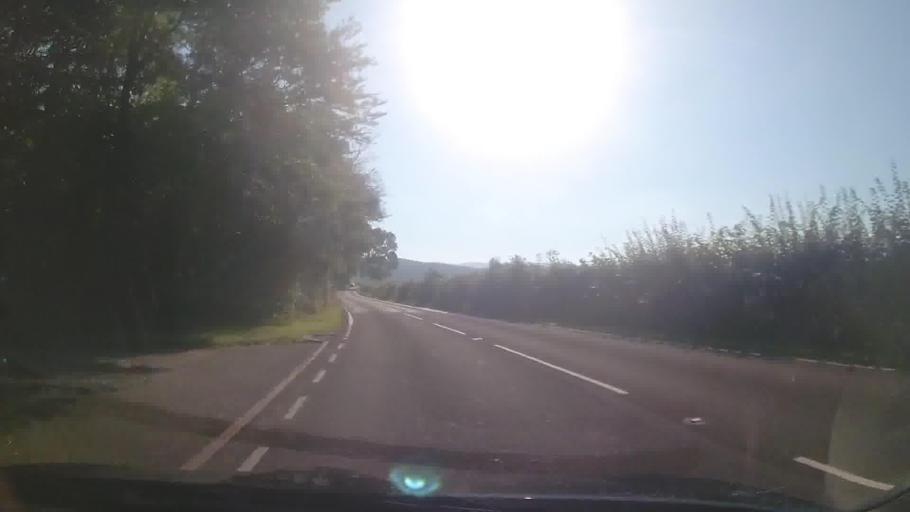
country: GB
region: England
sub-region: Cumbria
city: Seascale
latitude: 54.3753
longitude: -3.4140
